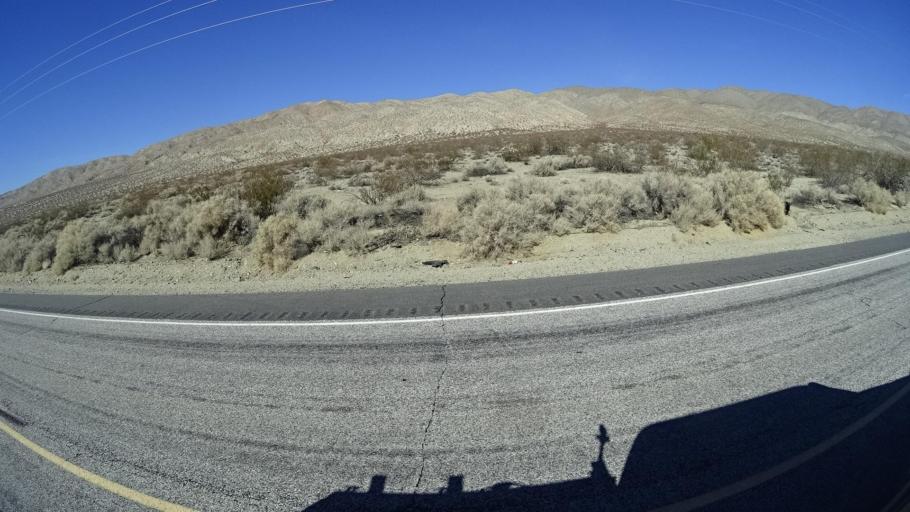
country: US
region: California
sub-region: Kern County
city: California City
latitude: 35.3721
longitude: -117.8763
